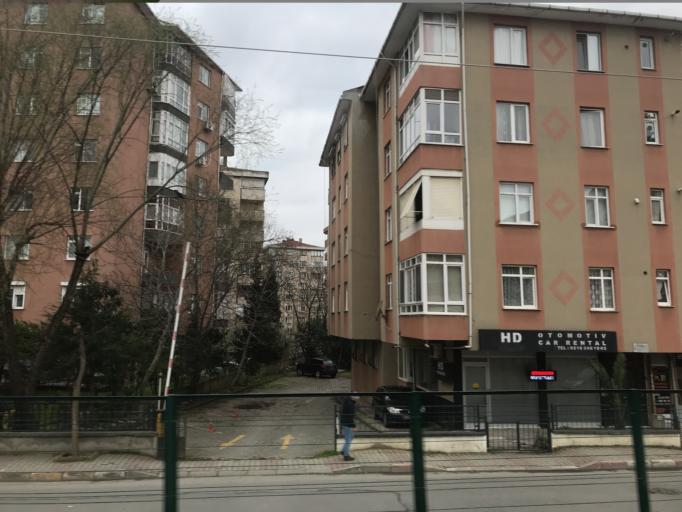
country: TR
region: Istanbul
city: Maltepe
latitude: 40.8996
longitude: 29.1681
